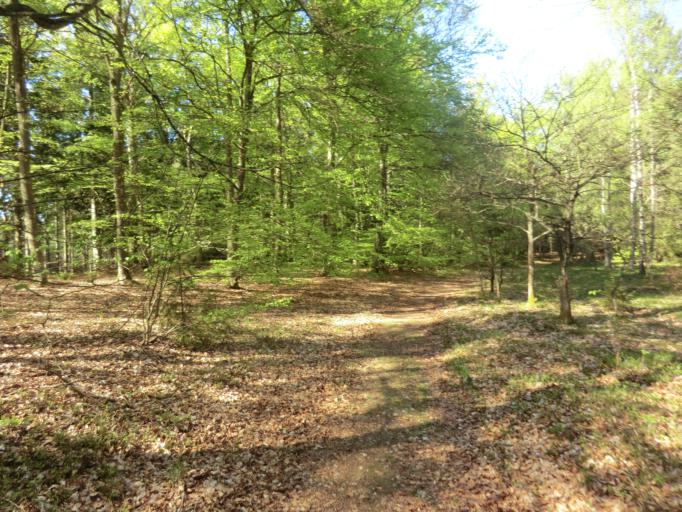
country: SE
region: Skane
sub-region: Sjobo Kommun
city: Sjoebo
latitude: 55.5731
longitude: 13.7146
